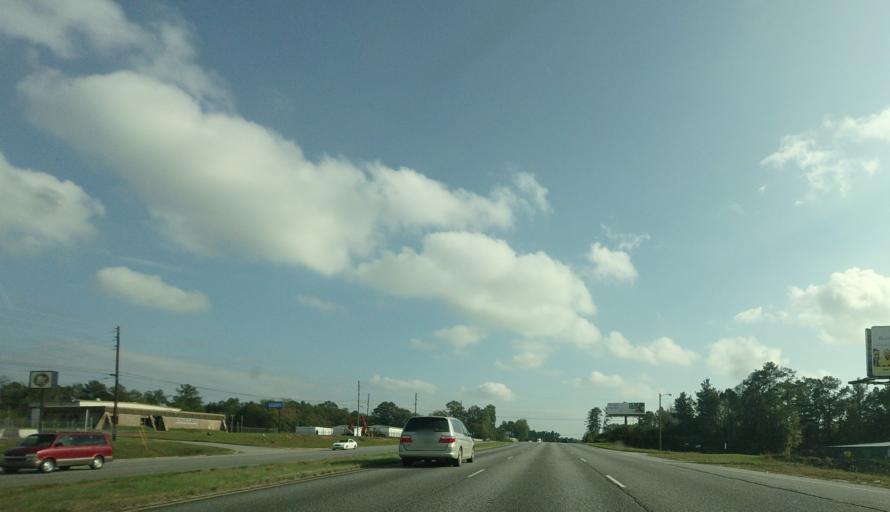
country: US
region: Georgia
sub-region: Bibb County
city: Macon
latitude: 32.7546
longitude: -83.6604
